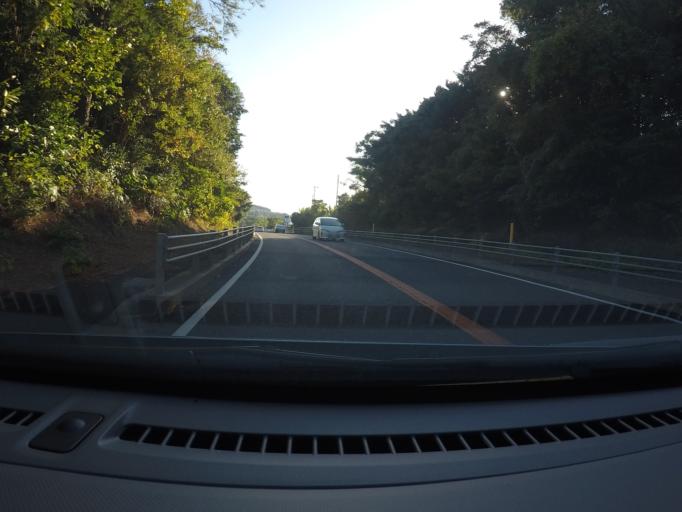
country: JP
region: Kumamoto
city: Minamata
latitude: 32.1584
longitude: 130.3642
